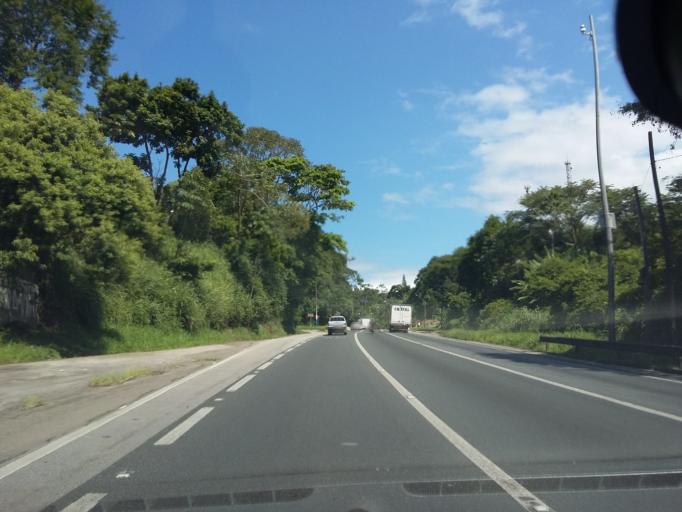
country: BR
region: Santa Catarina
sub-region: Itapema
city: Itapema
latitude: -27.0401
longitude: -48.5999
